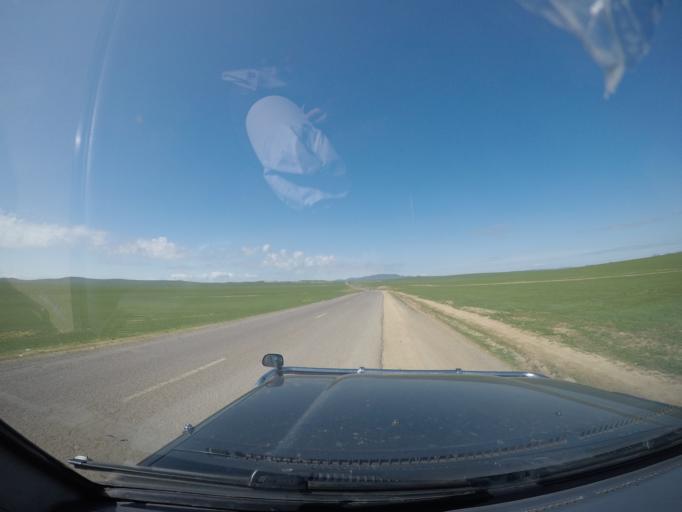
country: MN
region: Suhbaatar
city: Bayasgalant
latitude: 47.3435
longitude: 111.5804
